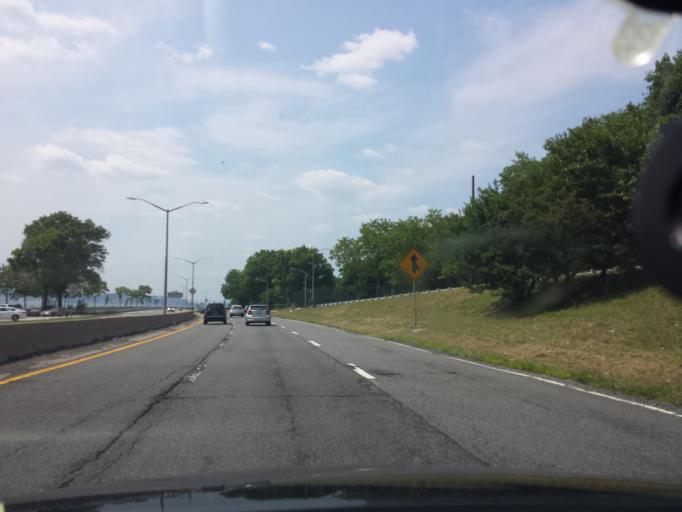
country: US
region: New York
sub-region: Kings County
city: Bensonhurst
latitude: 40.6113
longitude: -74.0363
